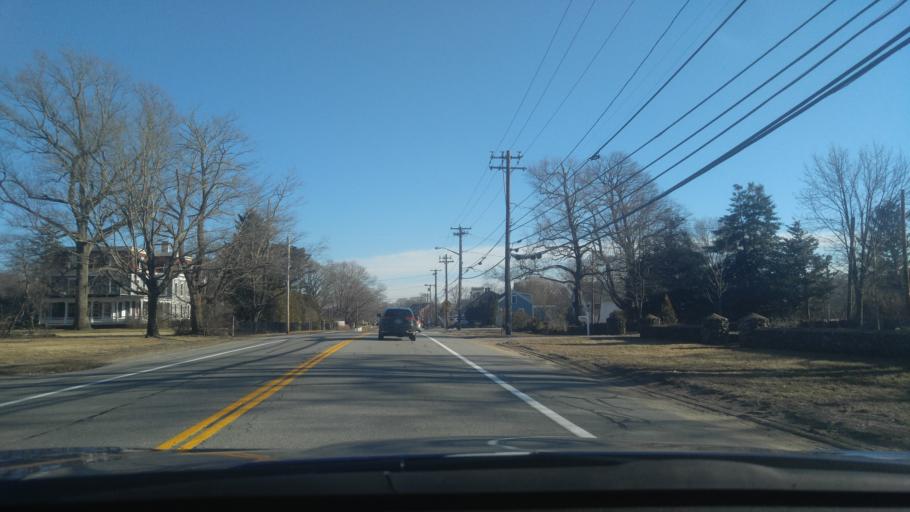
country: US
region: Rhode Island
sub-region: Washington County
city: North Kingstown
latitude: 41.5753
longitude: -71.4878
